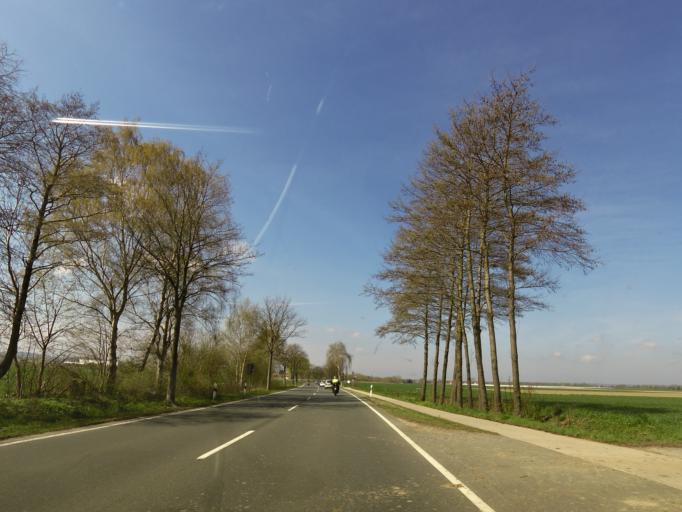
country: DE
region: Lower Saxony
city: Hagenburg
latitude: 52.4346
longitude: 9.3703
